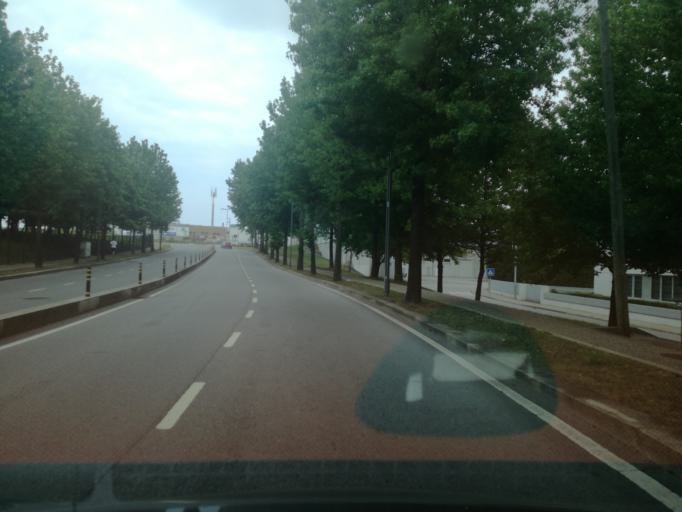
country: PT
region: Porto
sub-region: Maia
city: Anta
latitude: 41.2596
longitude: -8.6346
